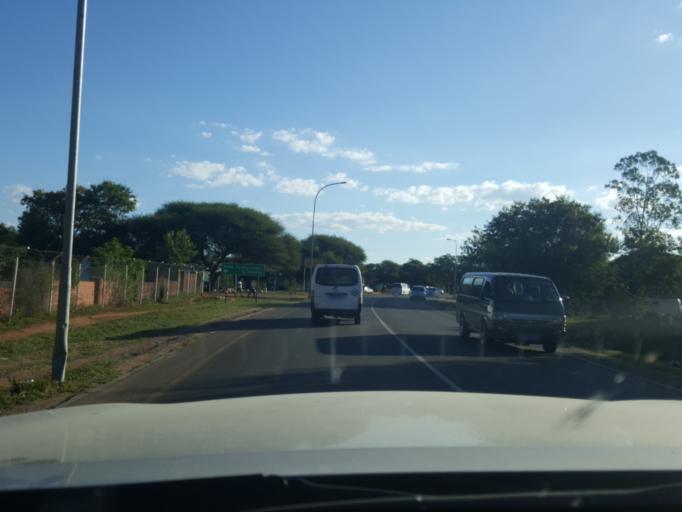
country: BW
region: South East
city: Gaborone
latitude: -24.6443
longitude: 25.9366
